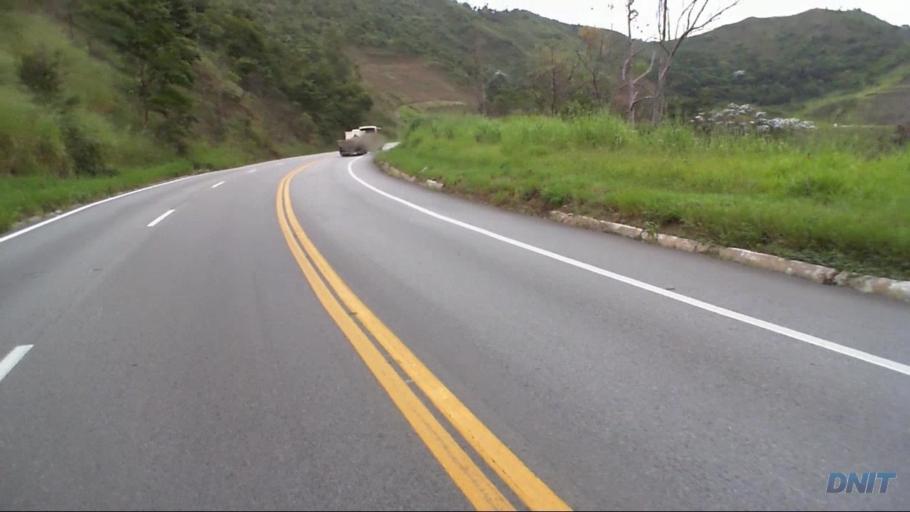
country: BR
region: Minas Gerais
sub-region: Nova Era
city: Nova Era
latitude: -19.6343
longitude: -42.8993
